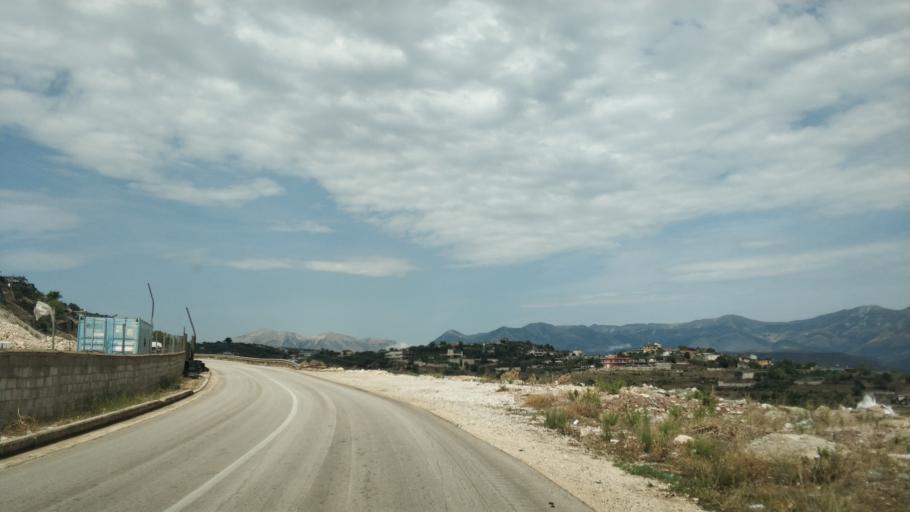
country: AL
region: Vlore
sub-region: Rrethi i Sarandes
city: Sarande
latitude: 39.8649
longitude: 20.0330
